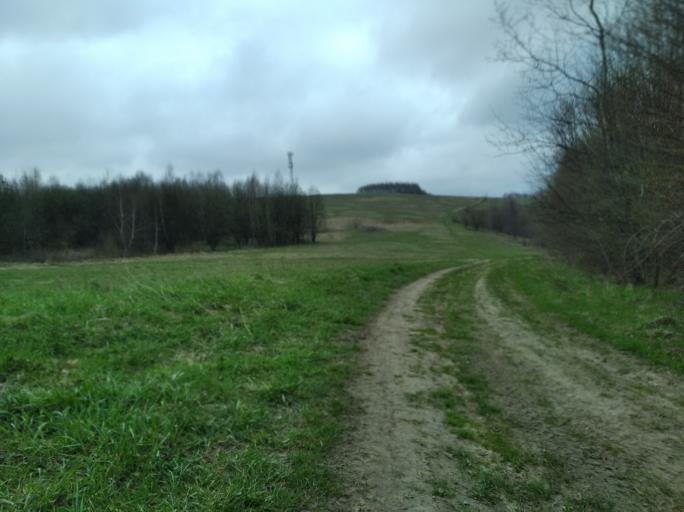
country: PL
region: Subcarpathian Voivodeship
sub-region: Powiat strzyzowski
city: Jawornik
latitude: 49.8159
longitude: 21.9015
